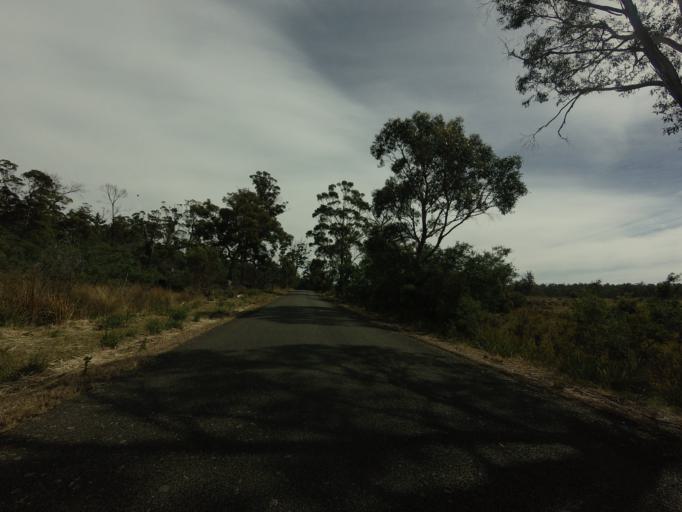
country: AU
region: Tasmania
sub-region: Sorell
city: Sorell
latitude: -42.5460
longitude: 147.6647
